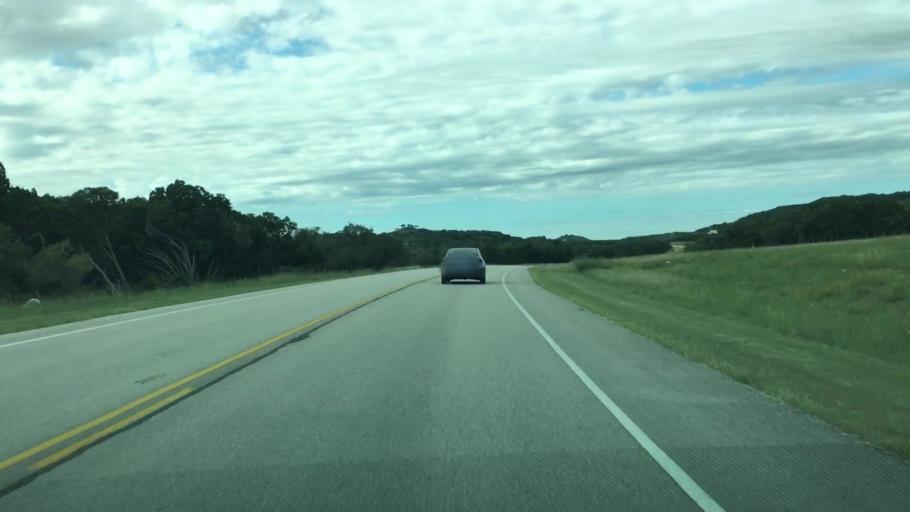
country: US
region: Texas
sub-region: Hays County
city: Wimberley
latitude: 30.0094
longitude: -98.0833
